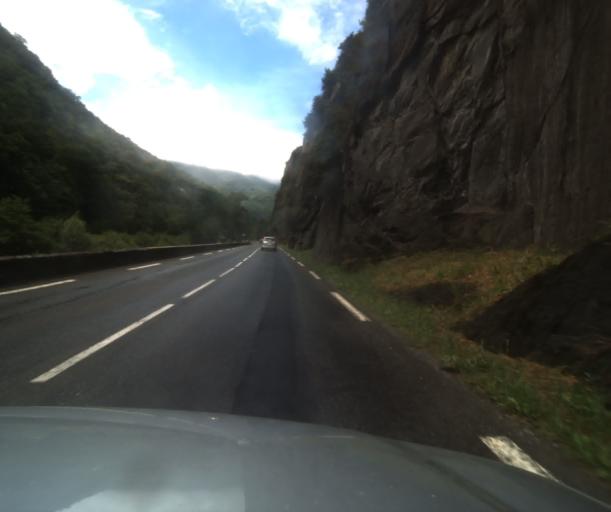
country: FR
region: Midi-Pyrenees
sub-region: Departement des Hautes-Pyrenees
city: Pierrefitte-Nestalas
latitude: 42.9481
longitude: -0.0604
